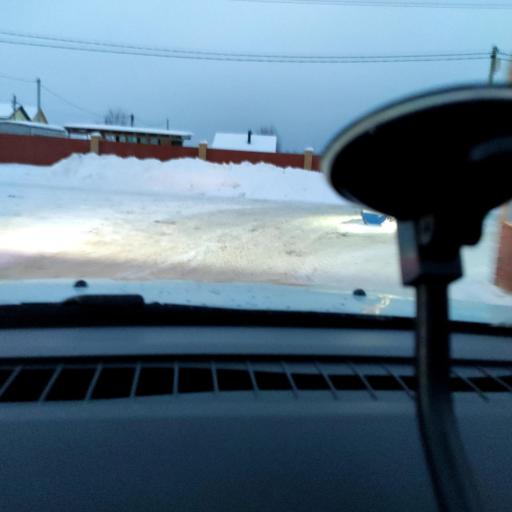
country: RU
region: Samara
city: Kurumoch
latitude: 53.4744
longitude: 50.0059
